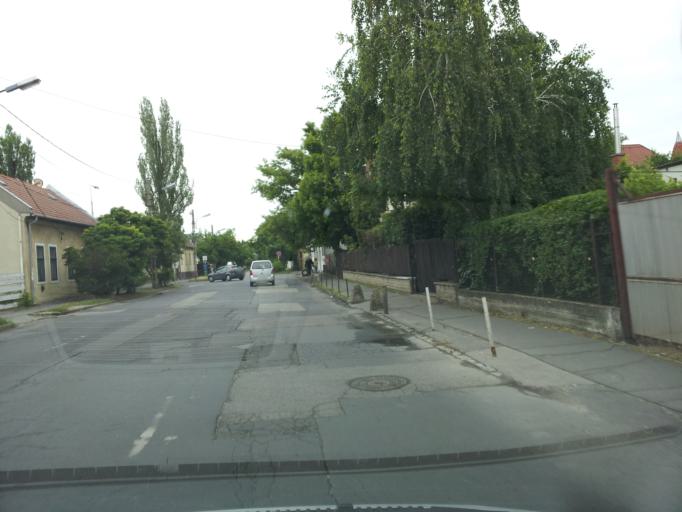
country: HU
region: Pest
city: Budakalasz
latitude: 47.5856
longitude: 19.0505
